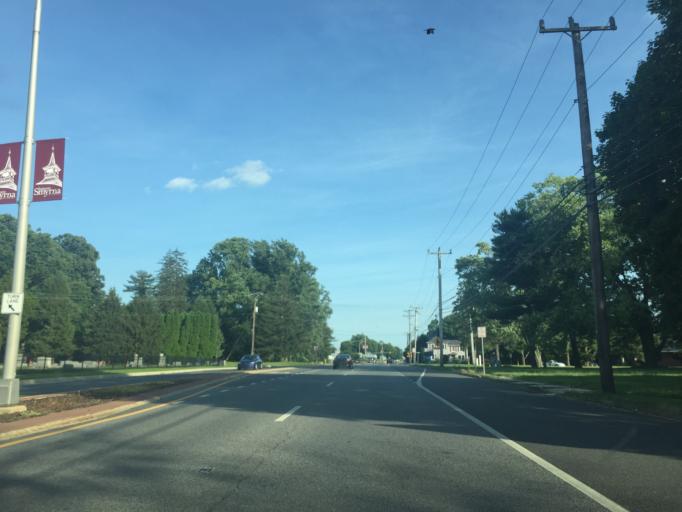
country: US
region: Delaware
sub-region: Kent County
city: Smyrna
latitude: 39.2946
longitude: -75.5984
